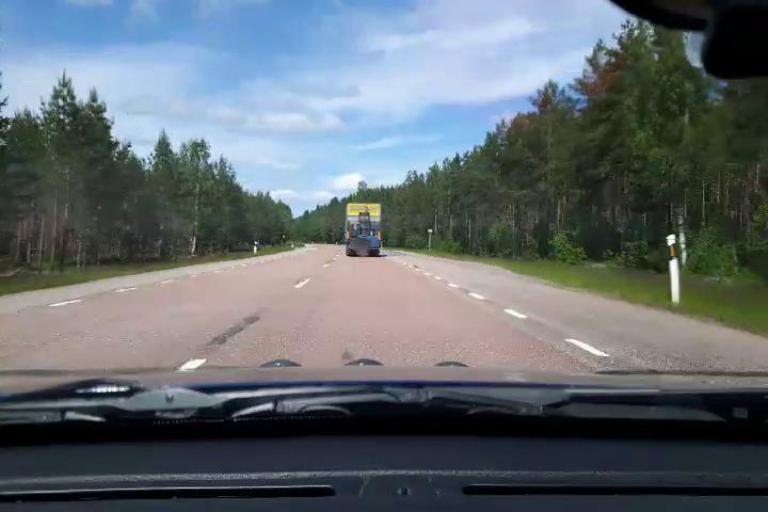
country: SE
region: Uppsala
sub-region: Osthammars Kommun
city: Bjorklinge
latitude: 60.1305
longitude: 17.5095
